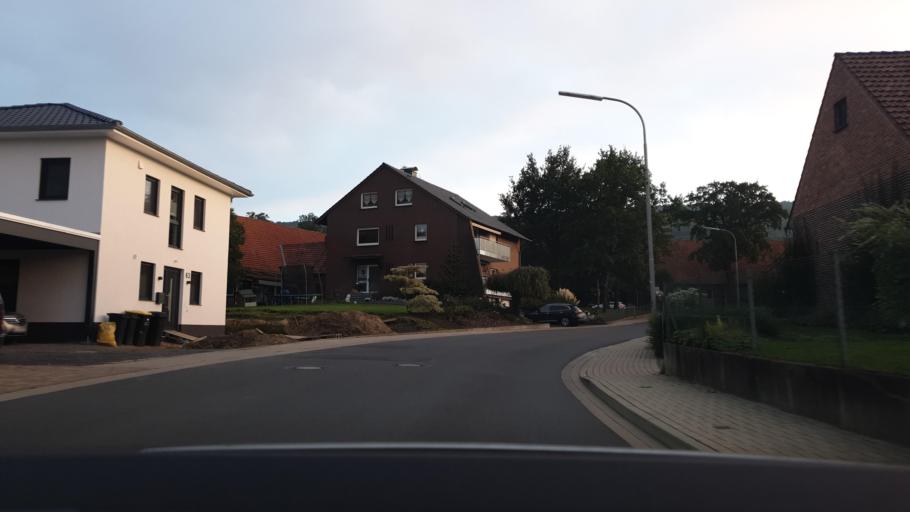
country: DE
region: North Rhine-Westphalia
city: Bad Oeynhausen
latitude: 52.2677
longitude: 8.8260
